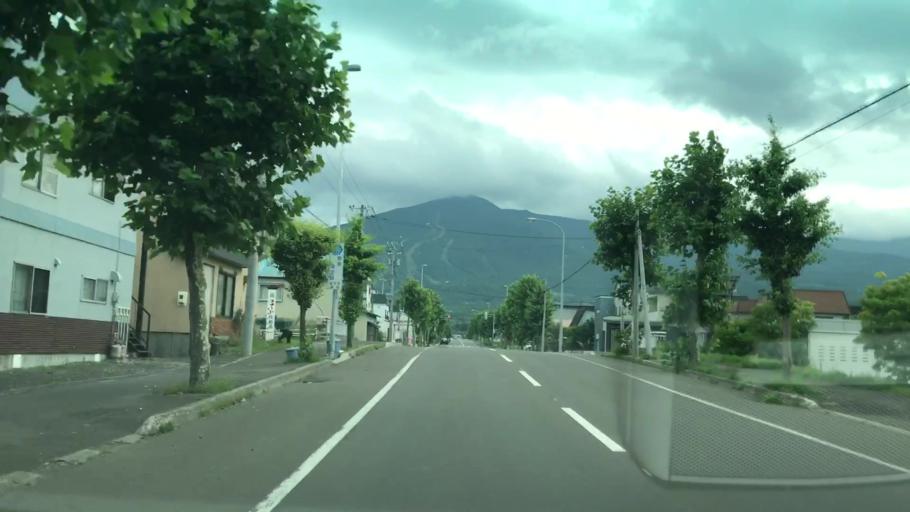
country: JP
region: Hokkaido
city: Iwanai
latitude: 42.9785
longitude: 140.5101
